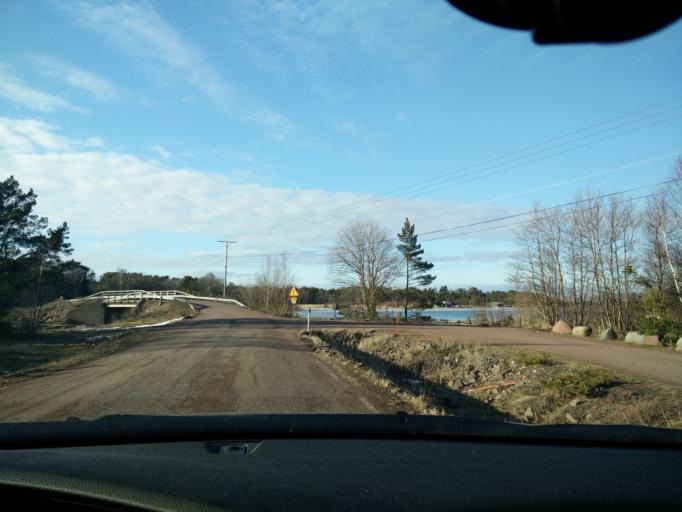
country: AX
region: Alands landsbygd
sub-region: Eckeroe
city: Eckeroe
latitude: 60.2413
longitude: 19.5378
